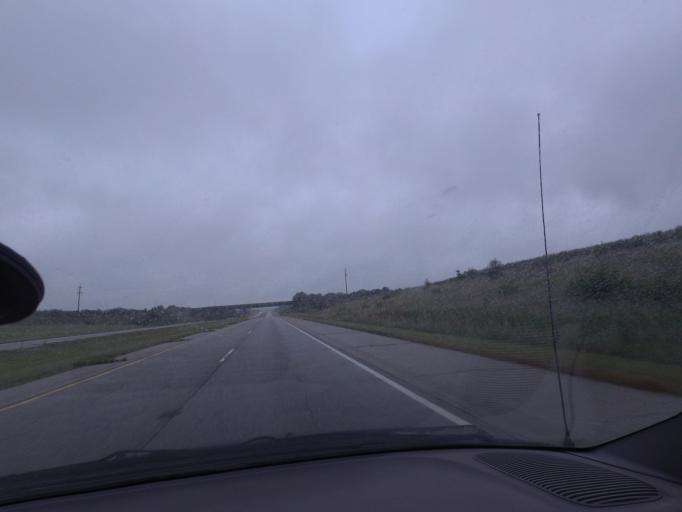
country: US
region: Illinois
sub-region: Pike County
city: Barry
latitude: 39.6925
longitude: -90.9750
